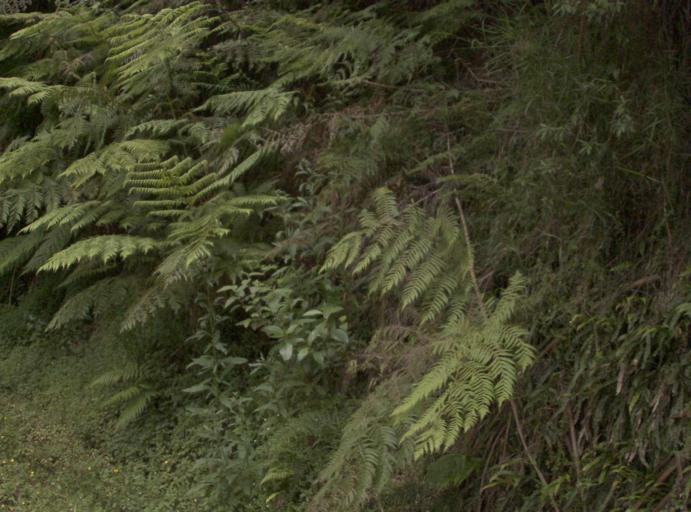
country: AU
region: Victoria
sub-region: Latrobe
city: Traralgon
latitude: -38.4553
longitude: 146.5448
